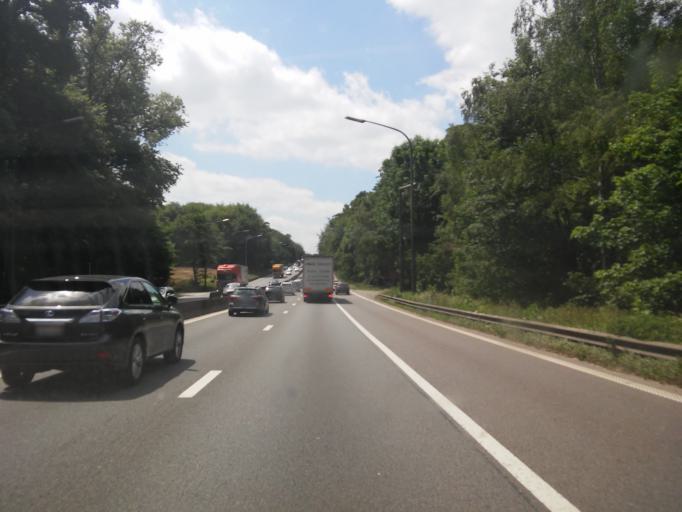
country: BE
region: Flanders
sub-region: Provincie Vlaams-Brabant
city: Wezembeek-Oppem
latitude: 50.8112
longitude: 4.4714
